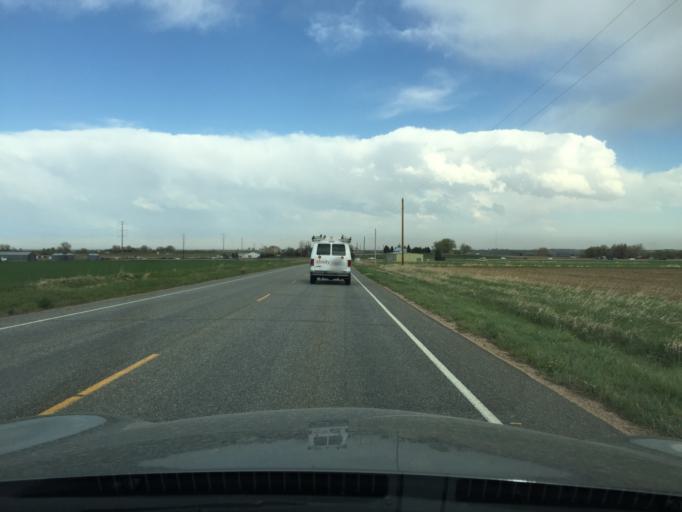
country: US
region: Colorado
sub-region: Boulder County
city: Erie
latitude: 40.0729
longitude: -105.1088
